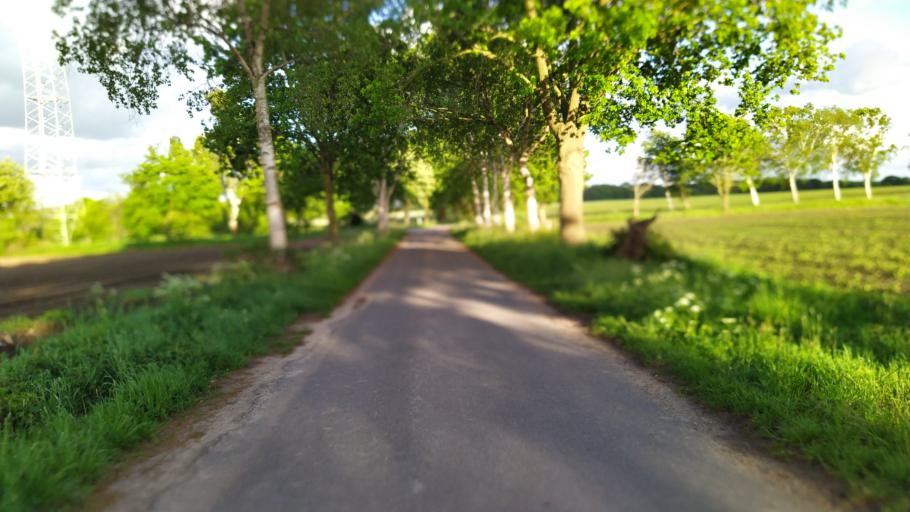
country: DE
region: Lower Saxony
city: Bargstedt
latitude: 53.4792
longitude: 9.4534
